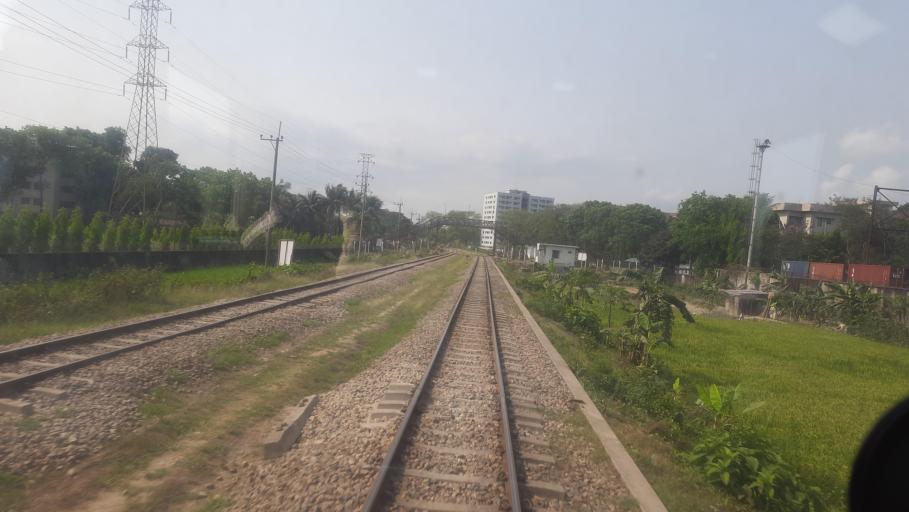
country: BD
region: Chittagong
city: Chittagong
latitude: 22.4177
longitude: 91.7540
